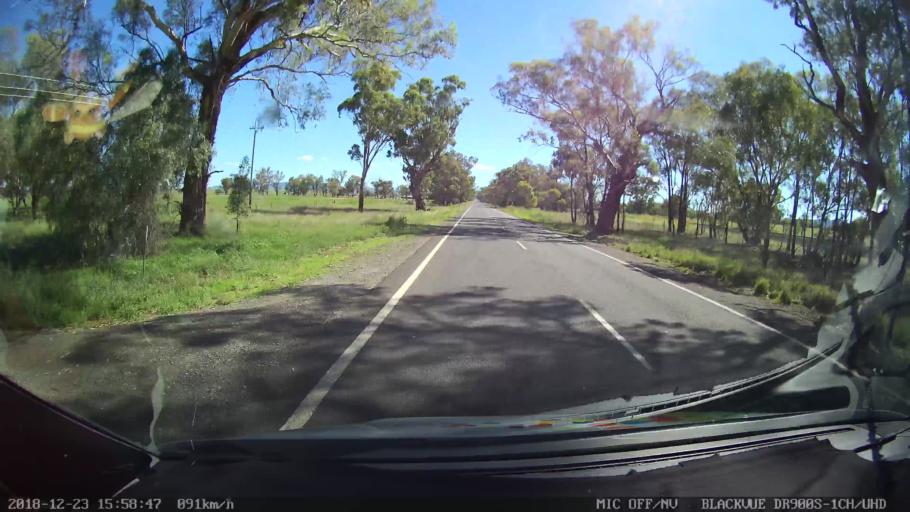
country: AU
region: New South Wales
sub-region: Tamworth Municipality
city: Phillip
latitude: -31.1923
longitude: 150.8387
